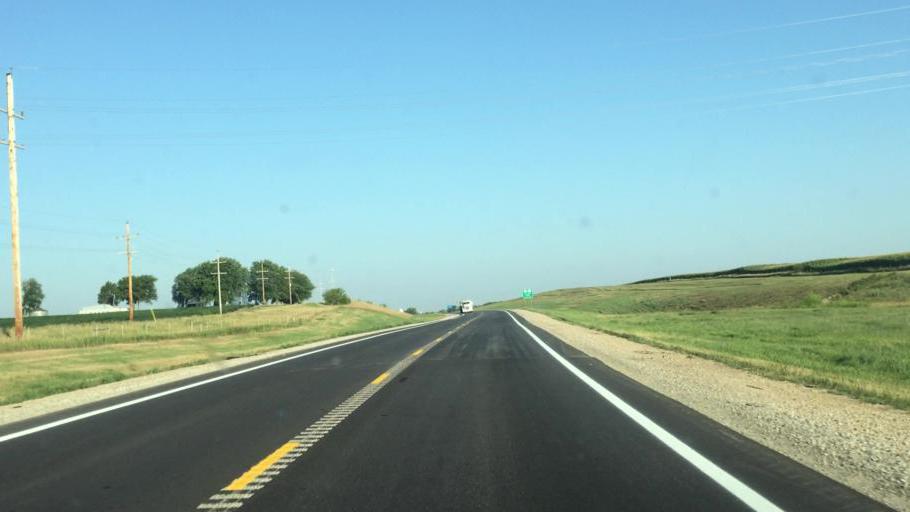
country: US
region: Kansas
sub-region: Brown County
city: Hiawatha
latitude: 39.8412
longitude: -95.5078
